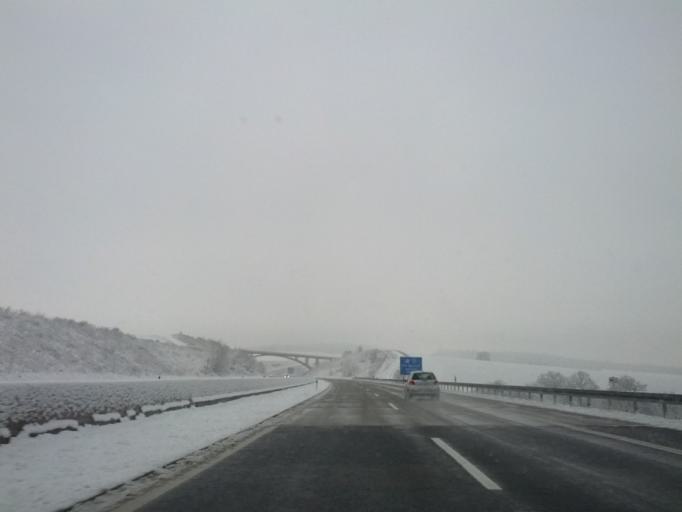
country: DE
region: Bavaria
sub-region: Regierungsbezirk Unterfranken
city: Rodelmaier
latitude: 50.3170
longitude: 10.2879
